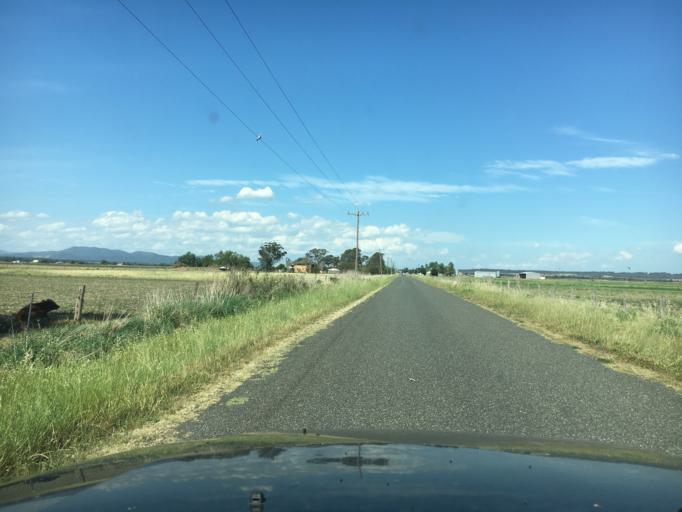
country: AU
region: New South Wales
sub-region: Singleton
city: Singleton
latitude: -32.6007
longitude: 151.2078
